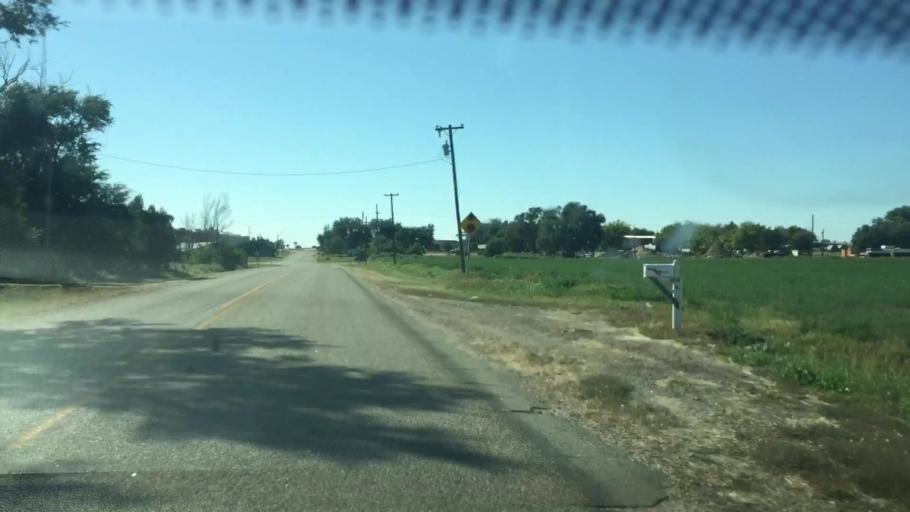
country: US
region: Colorado
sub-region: Prowers County
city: Lamar
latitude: 38.1167
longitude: -102.6157
